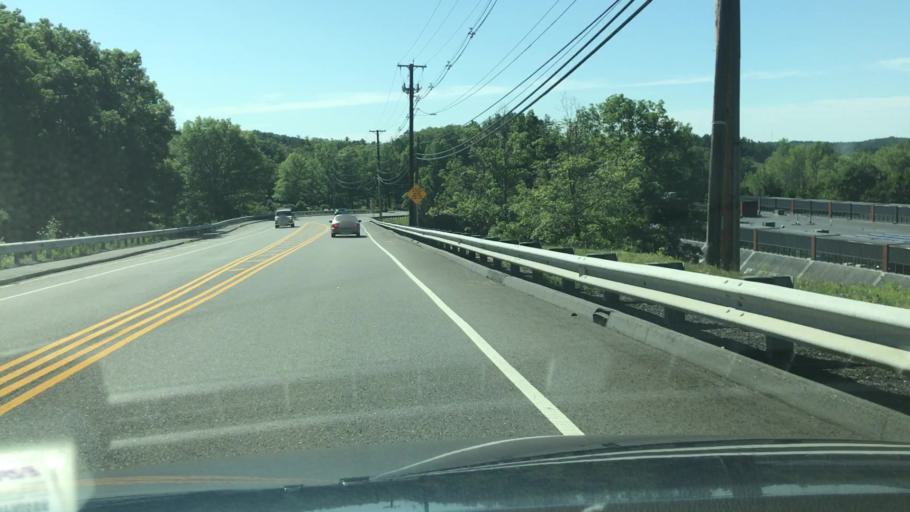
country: US
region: Massachusetts
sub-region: Middlesex County
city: Marlborough
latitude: 42.3254
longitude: -71.5805
